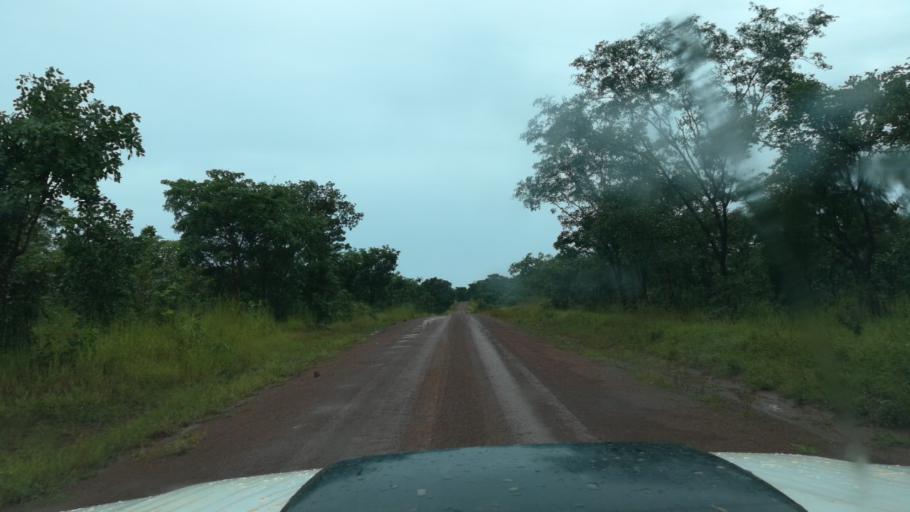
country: ZM
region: Luapula
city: Mwense
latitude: -10.3690
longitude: 28.1057
